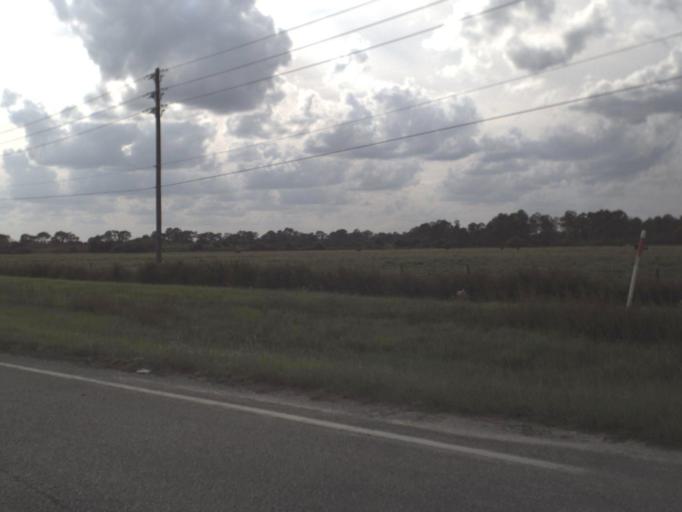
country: US
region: Florida
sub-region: Hendry County
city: LaBelle
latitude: 26.7185
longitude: -81.4975
